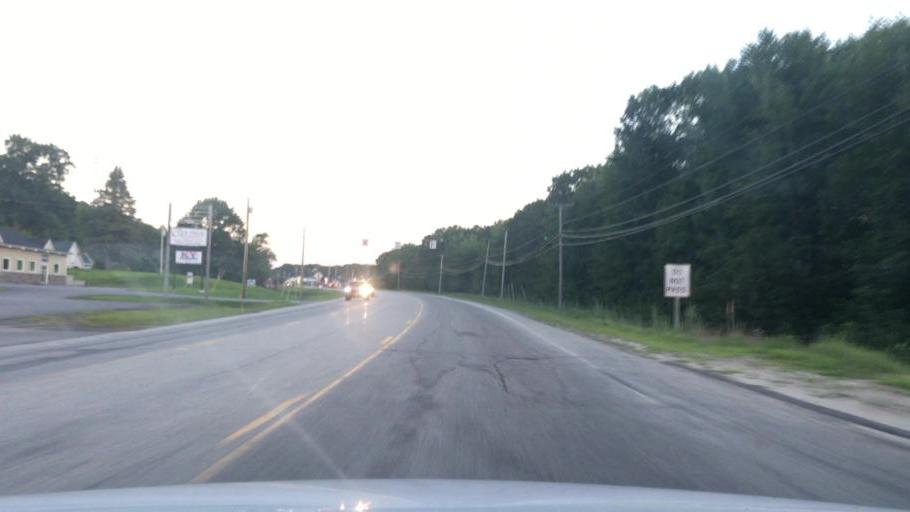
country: US
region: Maine
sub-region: Androscoggin County
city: Turner
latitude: 44.2026
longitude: -70.2454
